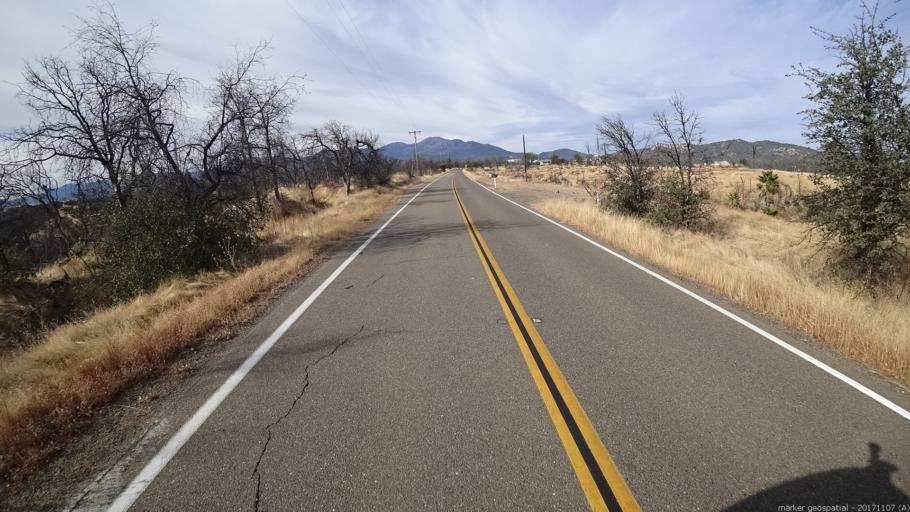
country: US
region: California
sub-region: Shasta County
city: Shasta
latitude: 40.4844
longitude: -122.5101
